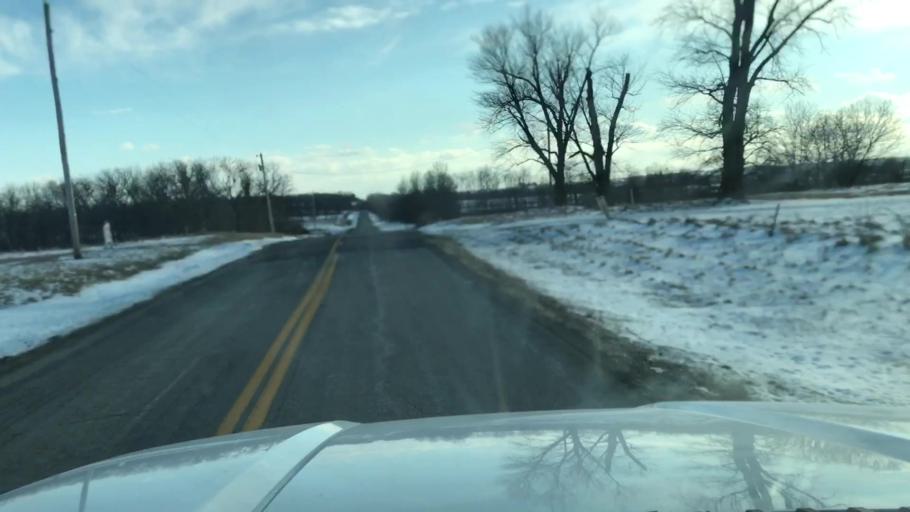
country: US
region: Missouri
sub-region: Holt County
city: Oregon
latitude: 40.1116
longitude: -95.0227
